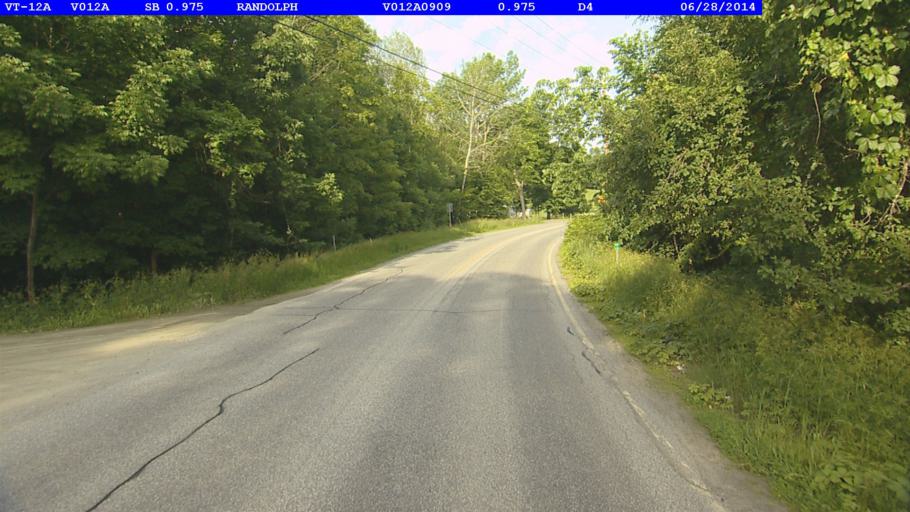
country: US
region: Vermont
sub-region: Orange County
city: Randolph
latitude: 43.9315
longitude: -72.6816
